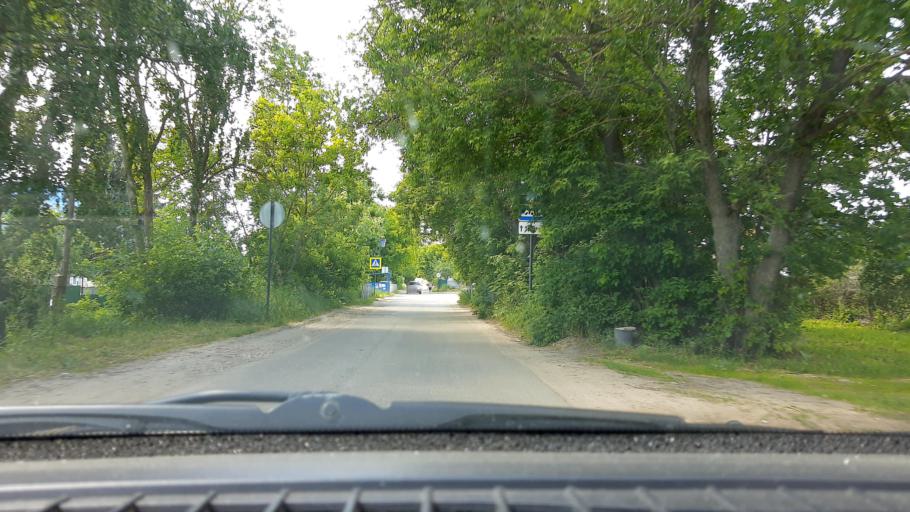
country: RU
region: Nizjnij Novgorod
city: Burevestnik
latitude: 56.1882
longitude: 43.9291
